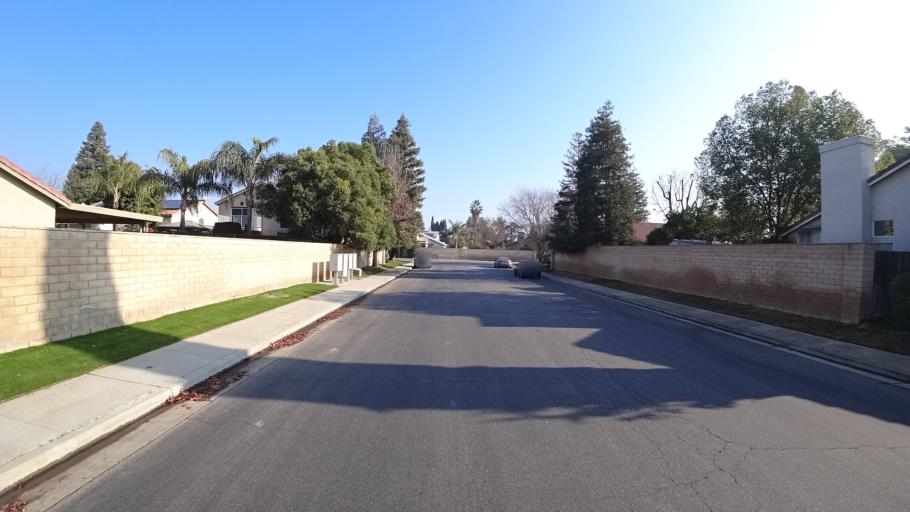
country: US
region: California
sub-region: Kern County
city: Greenacres
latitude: 35.3937
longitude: -119.1027
